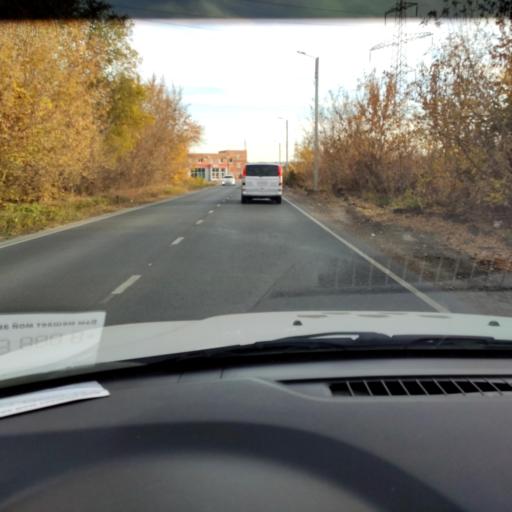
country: RU
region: Samara
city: Zhigulevsk
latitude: 53.5141
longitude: 49.4707
